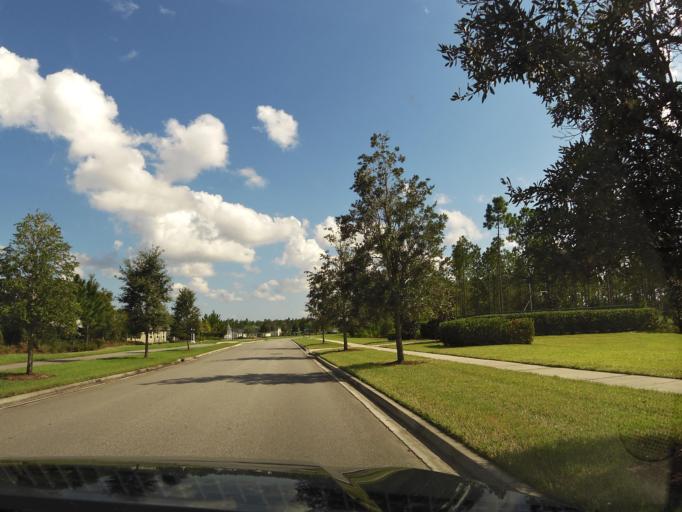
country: US
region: Florida
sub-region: Saint Johns County
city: Palm Valley
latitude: 30.0795
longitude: -81.4697
